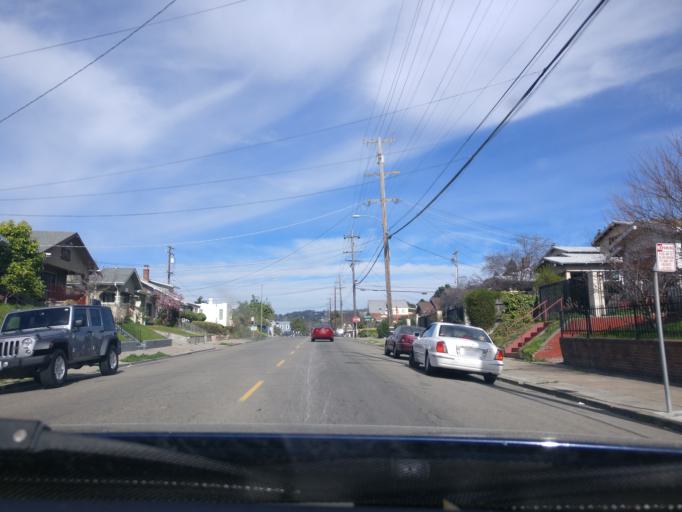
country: US
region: California
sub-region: Alameda County
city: Piedmont
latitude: 37.7947
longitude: -122.2264
